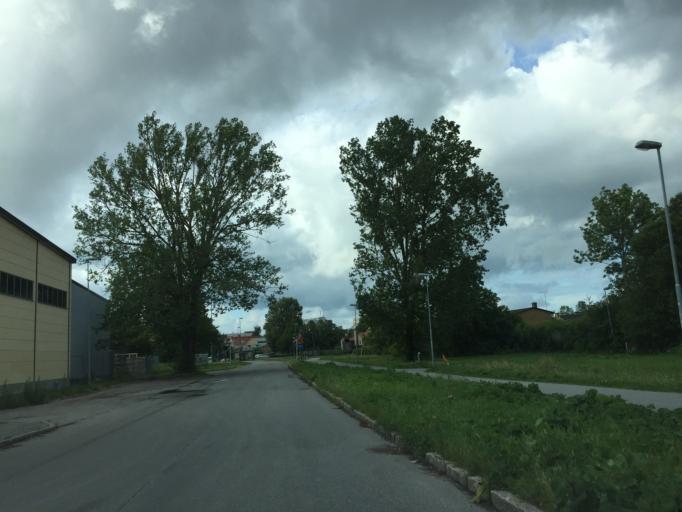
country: SE
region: OErebro
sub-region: Orebro Kommun
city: Orebro
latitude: 59.2618
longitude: 15.2098
